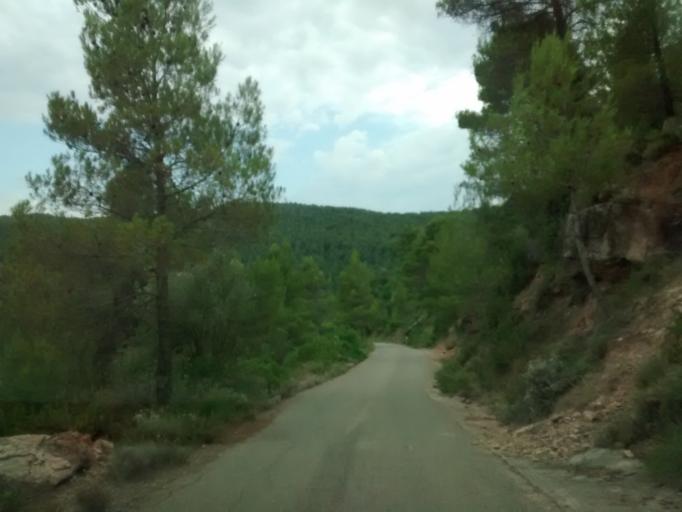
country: ES
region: Catalonia
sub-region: Provincia de Barcelona
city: Fonollosa
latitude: 41.7632
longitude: 1.6896
